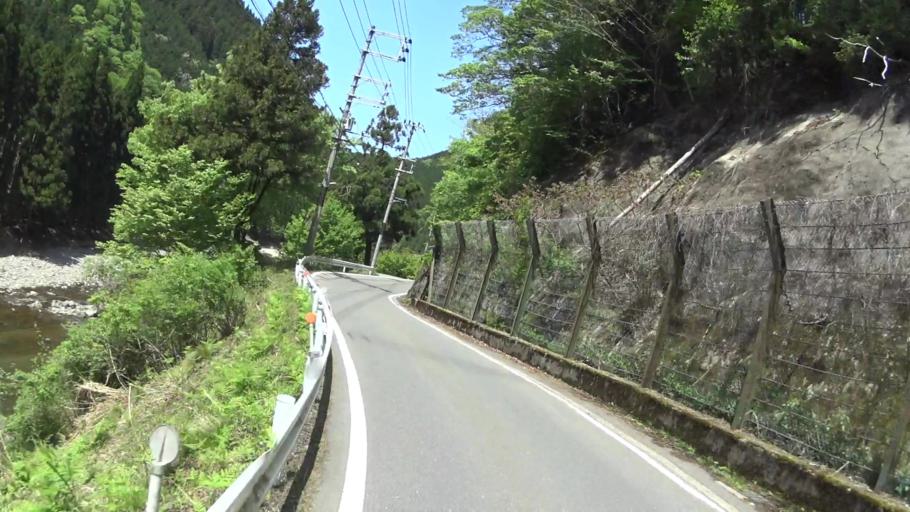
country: JP
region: Shiga Prefecture
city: Kitahama
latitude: 35.2069
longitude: 135.7588
